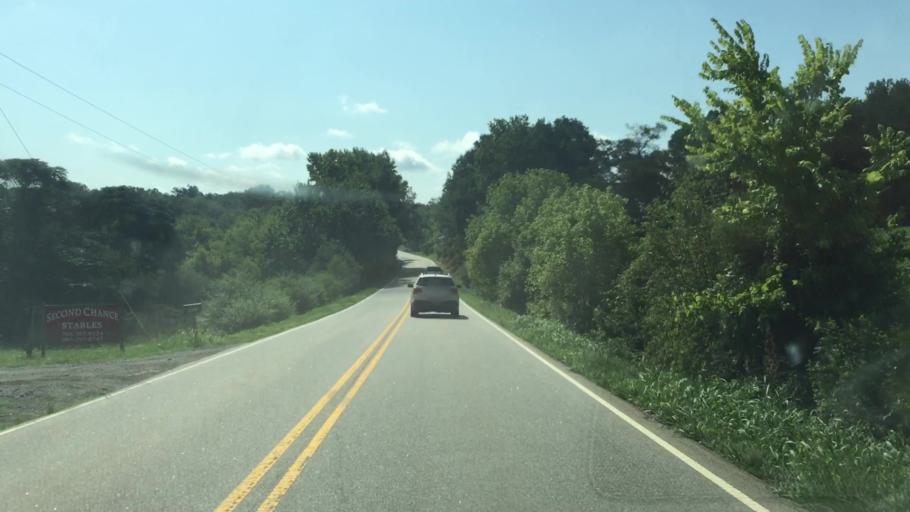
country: US
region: North Carolina
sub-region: Anson County
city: Burnsville
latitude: 35.0933
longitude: -80.3017
